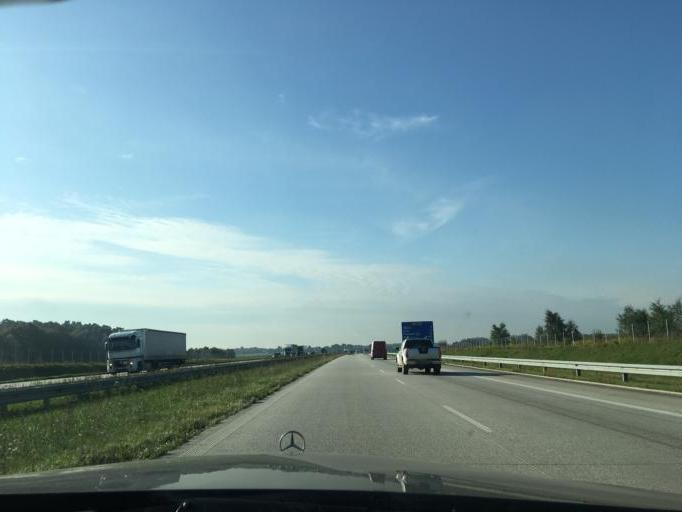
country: PL
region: Lodz Voivodeship
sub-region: Powiat lodzki wschodni
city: Andrespol
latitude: 51.7910
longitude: 19.6168
